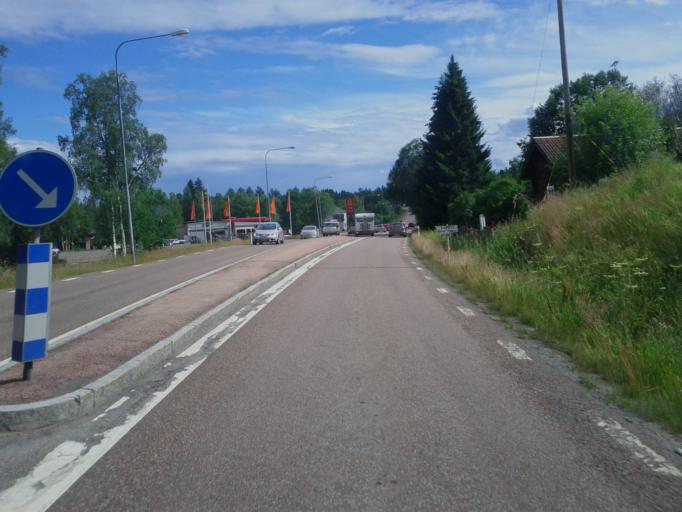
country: SE
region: Dalarna
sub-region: Faluns Kommun
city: Bjursas
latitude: 60.7349
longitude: 15.4372
